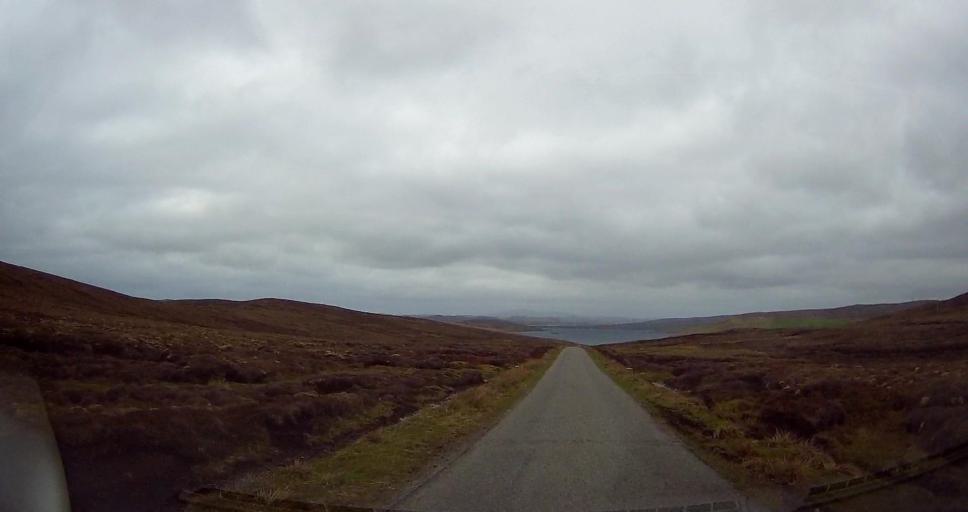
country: GB
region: Scotland
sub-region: Shetland Islands
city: Lerwick
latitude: 60.3215
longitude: -1.3378
